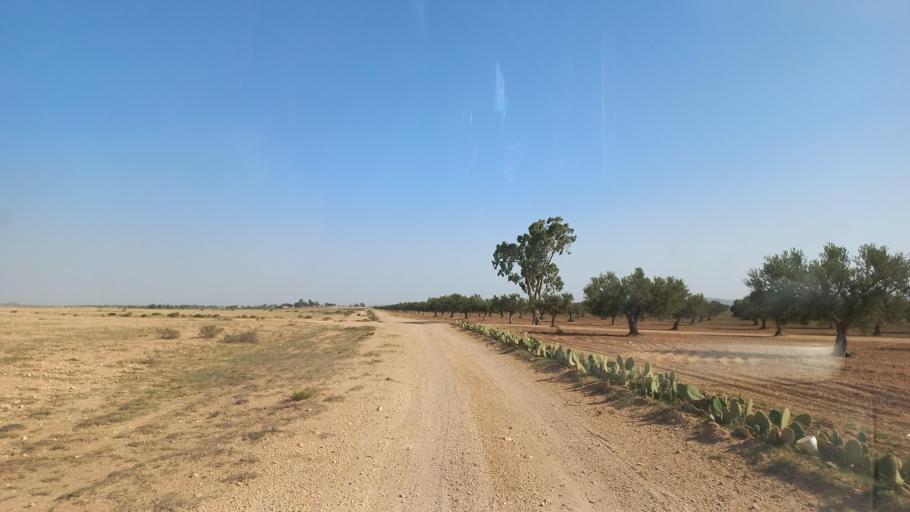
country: TN
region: Al Qasrayn
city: Kasserine
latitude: 35.3084
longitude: 9.0207
